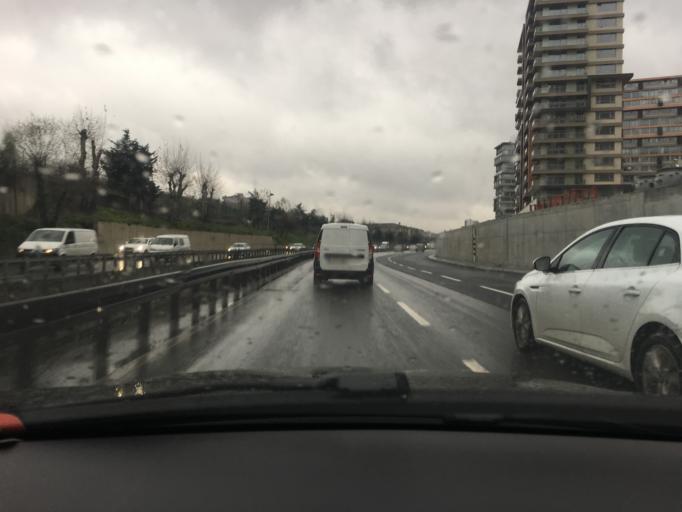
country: TR
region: Istanbul
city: merter keresteciler
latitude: 41.0230
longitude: 28.9000
